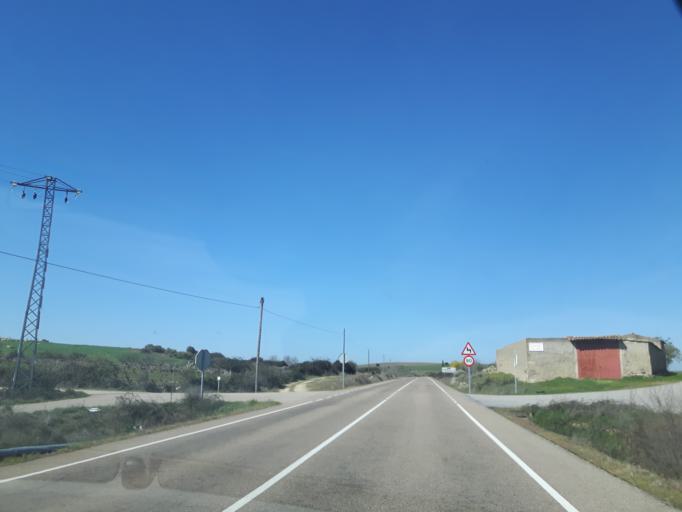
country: ES
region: Castille and Leon
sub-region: Provincia de Salamanca
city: Cerralbo
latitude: 40.9728
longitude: -6.5917
